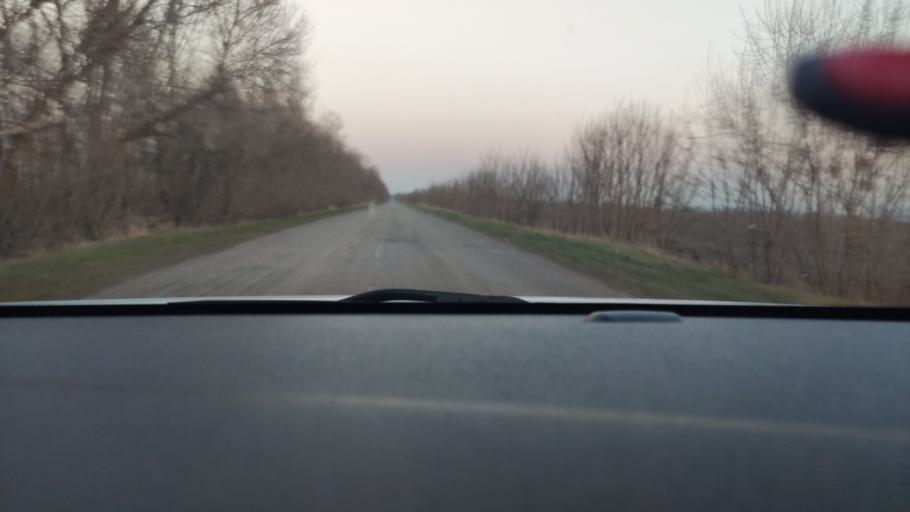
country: RU
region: Voronezj
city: Uryv-Pokrovka
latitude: 51.1432
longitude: 39.0698
